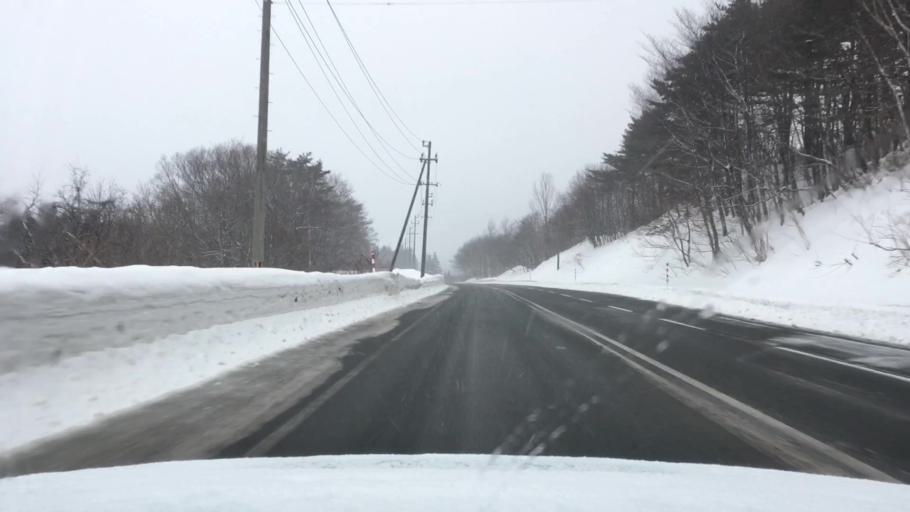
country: JP
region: Akita
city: Hanawa
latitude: 40.0204
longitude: 140.9883
